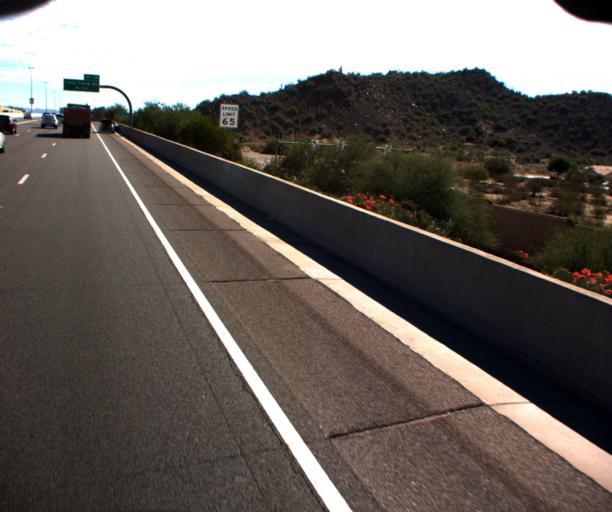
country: US
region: Arizona
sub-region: Maricopa County
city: Paradise Valley
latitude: 33.6689
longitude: -112.0504
